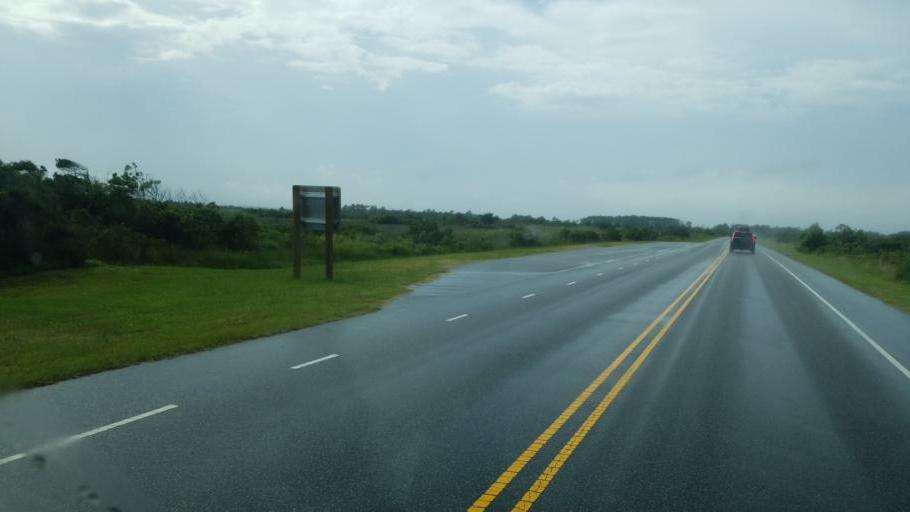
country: US
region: North Carolina
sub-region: Dare County
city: Wanchese
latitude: 35.8848
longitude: -75.5890
